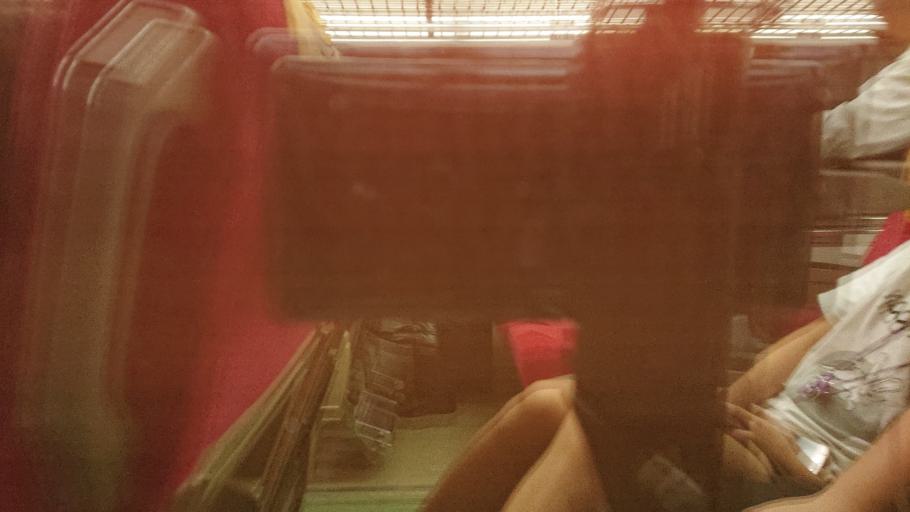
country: TW
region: Taiwan
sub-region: Keelung
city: Keelung
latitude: 25.1066
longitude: 121.8230
